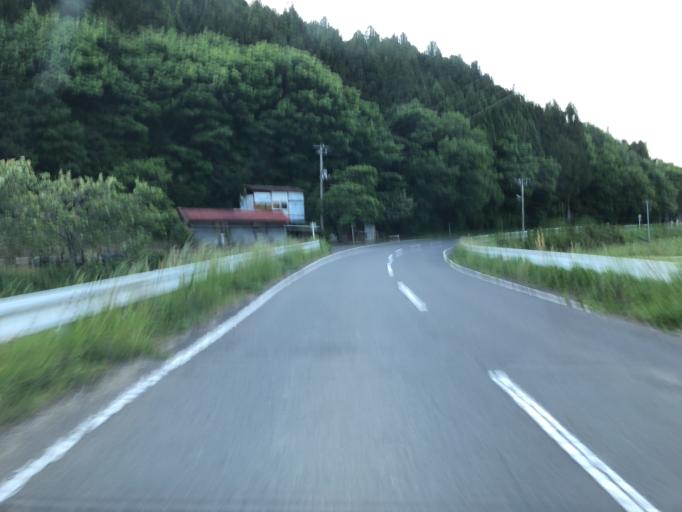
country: JP
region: Fukushima
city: Ishikawa
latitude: 36.9930
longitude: 140.4385
